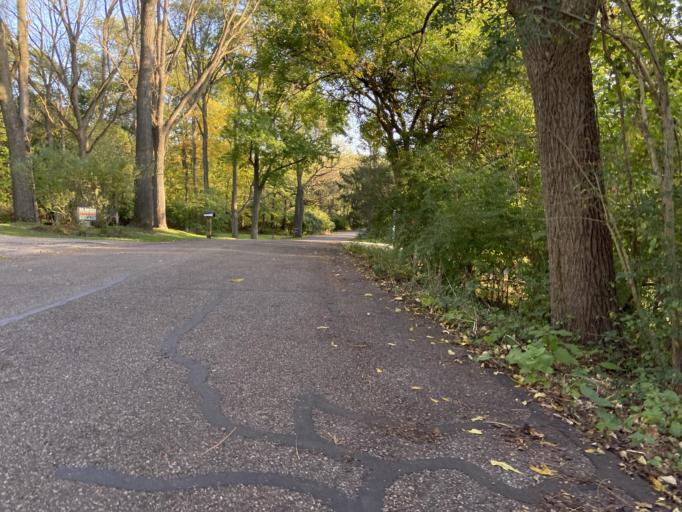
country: US
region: Michigan
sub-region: Oakland County
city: Franklin
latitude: 42.5076
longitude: -83.3325
